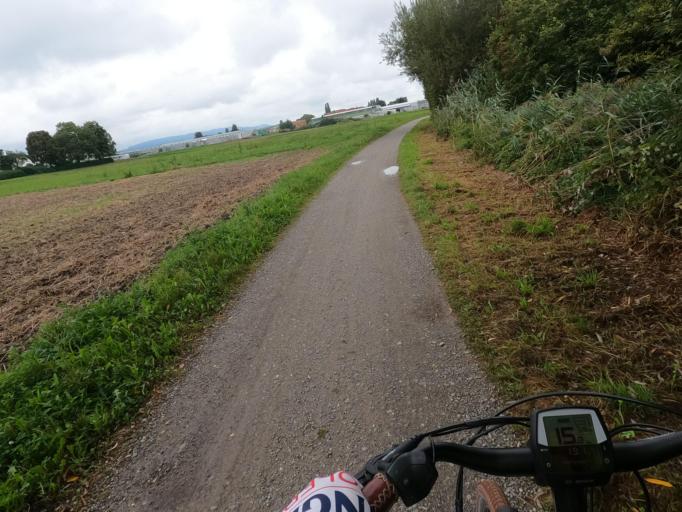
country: DE
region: Baden-Wuerttemberg
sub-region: Freiburg Region
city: Reichenau
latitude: 47.7017
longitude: 9.0535
